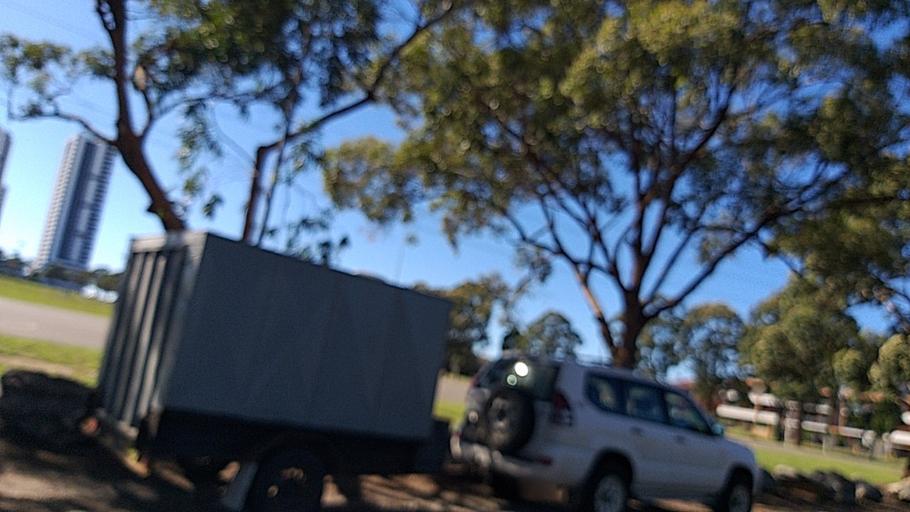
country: AU
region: New South Wales
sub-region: Liverpool
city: Miller
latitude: -33.9273
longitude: 150.9132
